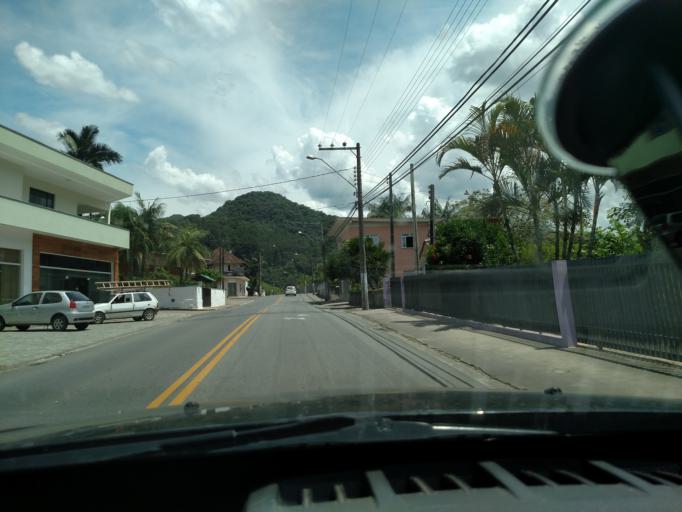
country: BR
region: Santa Catarina
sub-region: Blumenau
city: Blumenau
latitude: -26.9843
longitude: -49.0785
